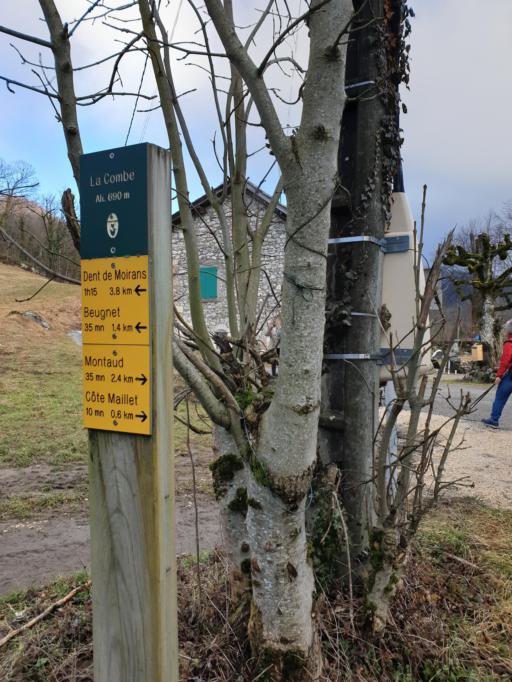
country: FR
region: Rhone-Alpes
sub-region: Departement de l'Isere
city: Saint-Quentin-sur-Isere
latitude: 45.2659
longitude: 5.5760
